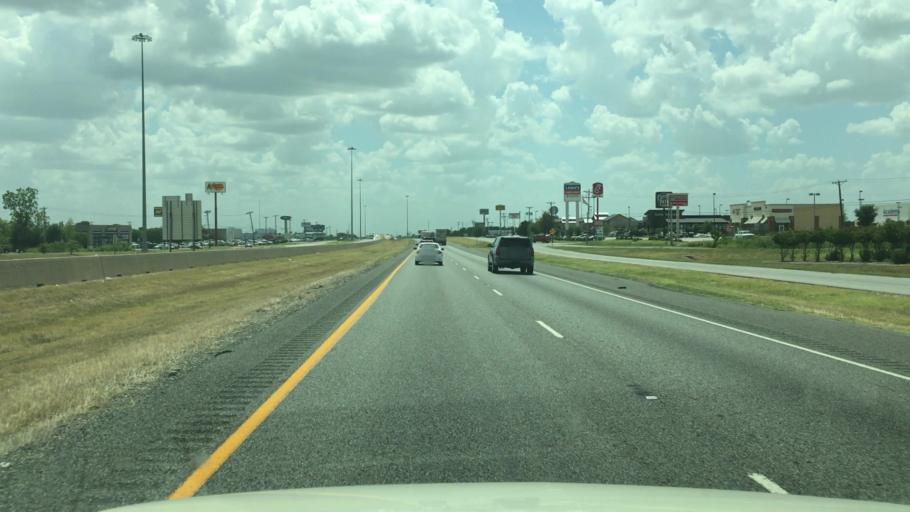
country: US
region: Texas
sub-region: Hunt County
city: Greenville
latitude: 33.0962
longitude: -96.1105
